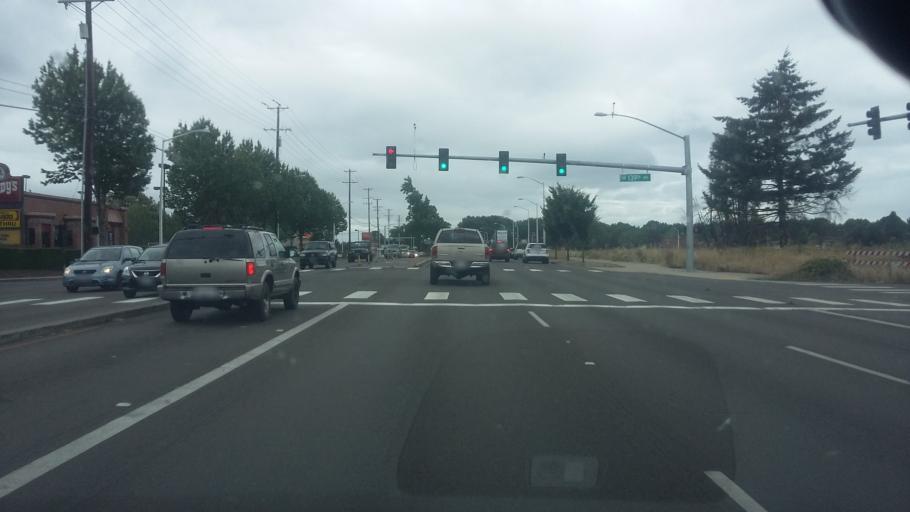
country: US
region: Washington
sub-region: Clark County
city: Mill Plain
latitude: 45.6183
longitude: -122.5290
